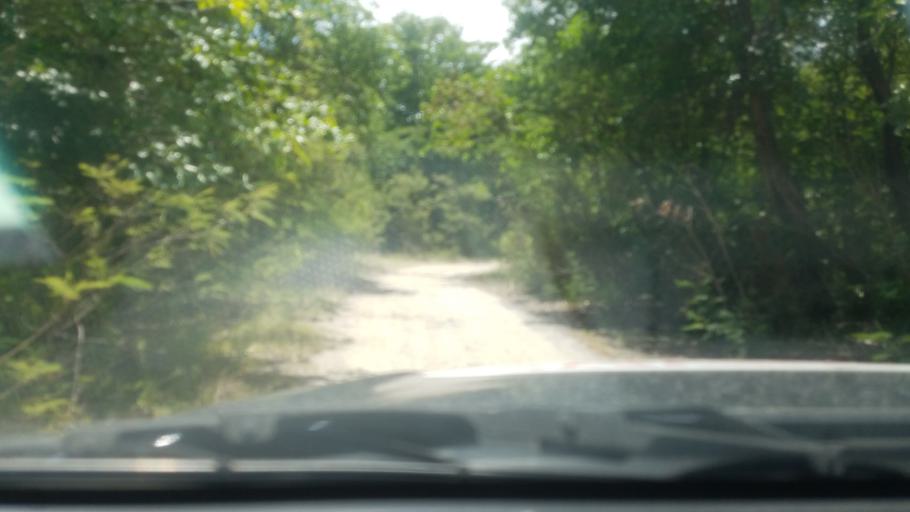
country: LC
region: Vieux-Fort
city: Vieux Fort
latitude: 13.7465
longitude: -60.9377
